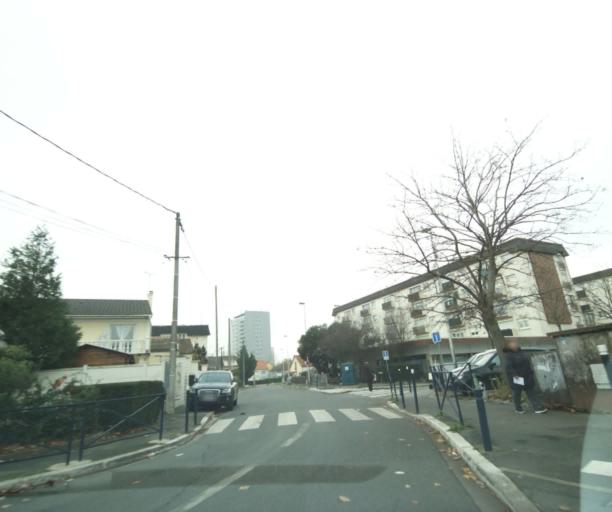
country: FR
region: Ile-de-France
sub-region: Departement de Seine-Saint-Denis
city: Villemomble
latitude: 48.8883
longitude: 2.4946
